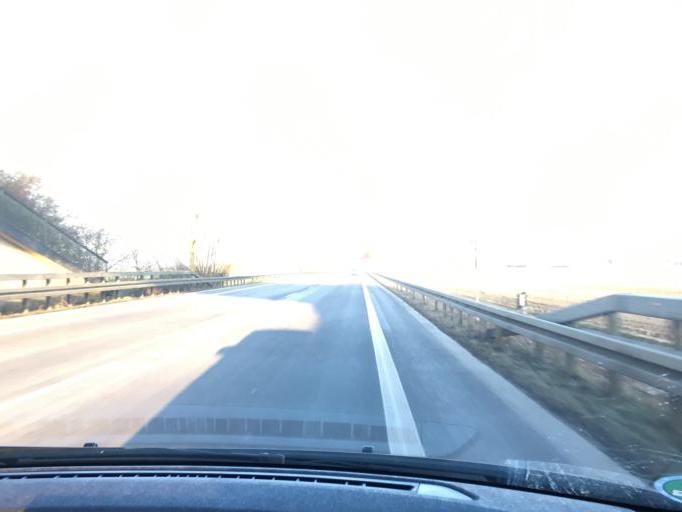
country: DE
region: North Rhine-Westphalia
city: Julich
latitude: 50.9476
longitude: 6.3953
